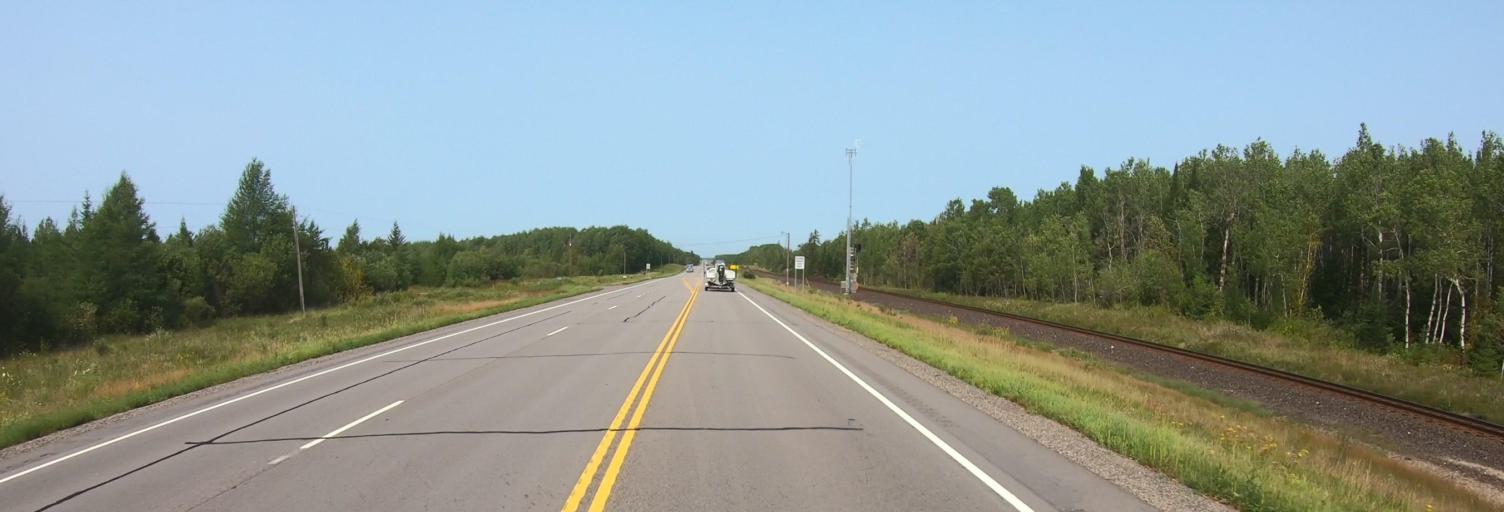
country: CA
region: Ontario
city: Fort Frances
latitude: 48.4471
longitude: -93.2655
